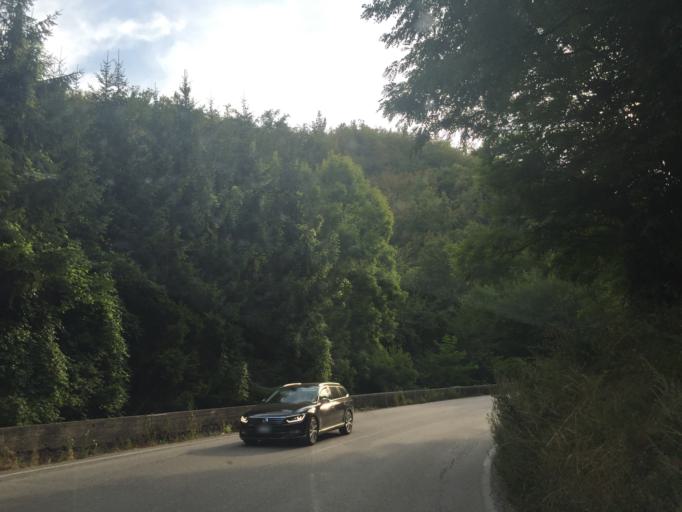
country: IT
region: Tuscany
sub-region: Provincia di Pistoia
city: Campo Tizzoro
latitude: 44.0058
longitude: 10.8398
